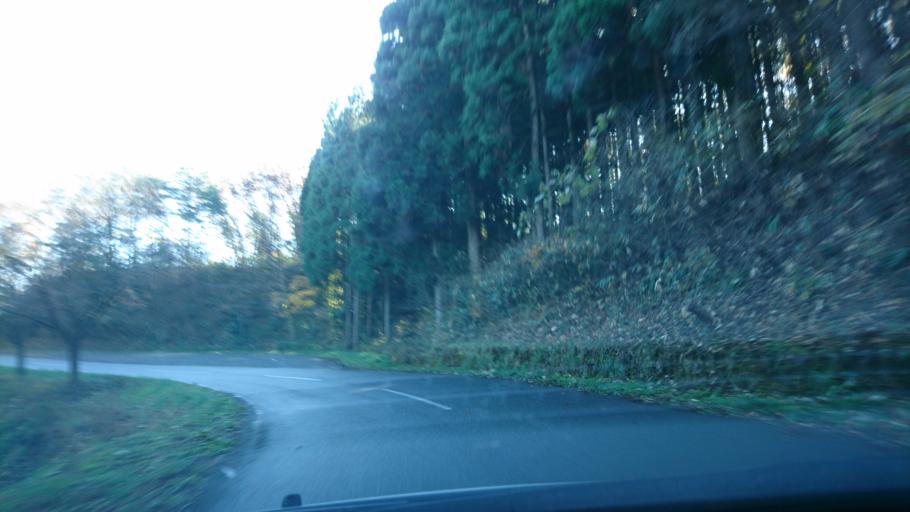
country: JP
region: Iwate
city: Ichinoseki
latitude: 38.9922
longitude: 141.0964
